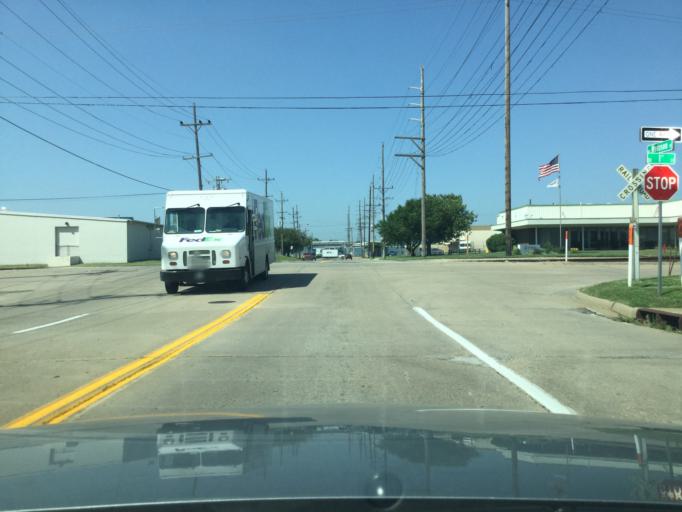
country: US
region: Kansas
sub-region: Shawnee County
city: Topeka
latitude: 39.0573
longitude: -95.6661
